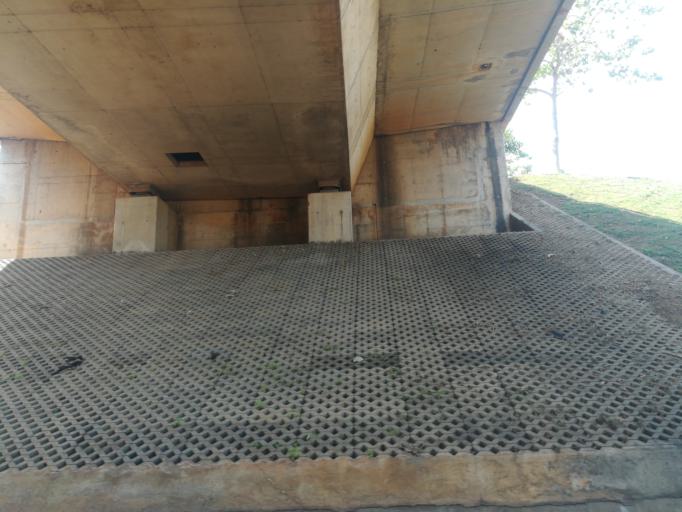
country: NG
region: Abuja Federal Capital Territory
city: Abuja
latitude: 9.0764
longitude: 7.4372
